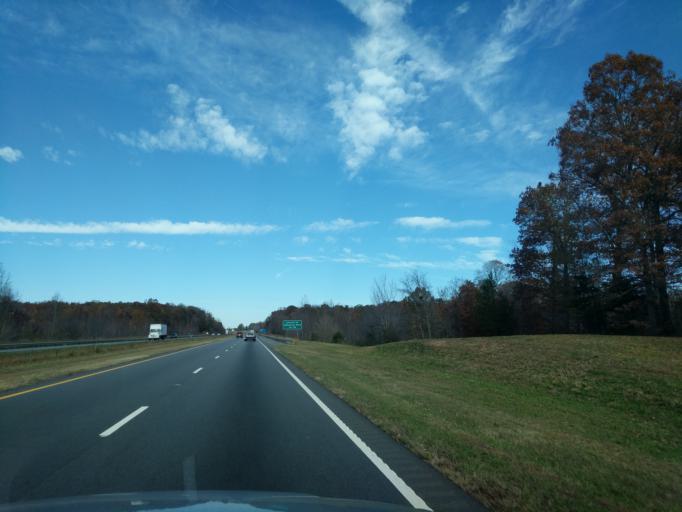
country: US
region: North Carolina
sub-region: Lincoln County
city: Lincolnton
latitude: 35.5156
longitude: -81.2228
